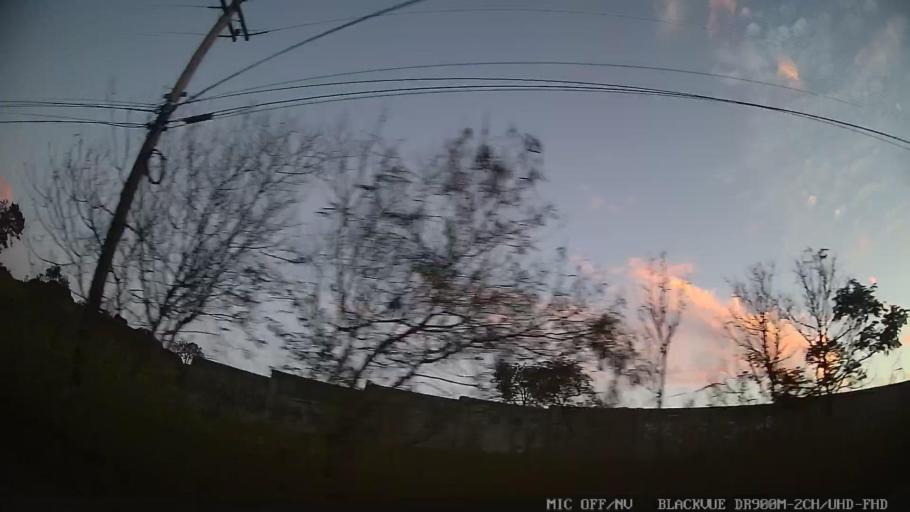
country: BR
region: Sao Paulo
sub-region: Itupeva
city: Itupeva
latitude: -23.1670
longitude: -47.1371
